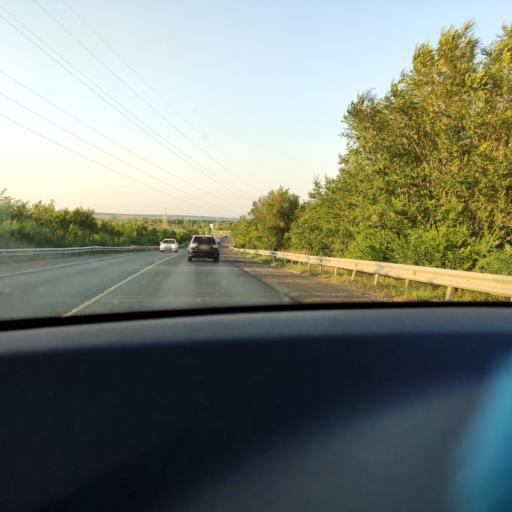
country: RU
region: Samara
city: Kinel'
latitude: 53.2437
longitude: 50.5835
